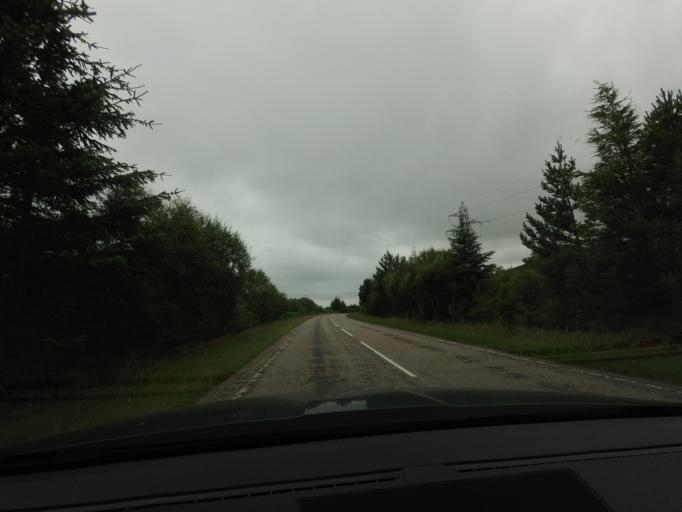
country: GB
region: Scotland
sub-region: Highland
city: Alness
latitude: 57.9924
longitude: -4.4040
